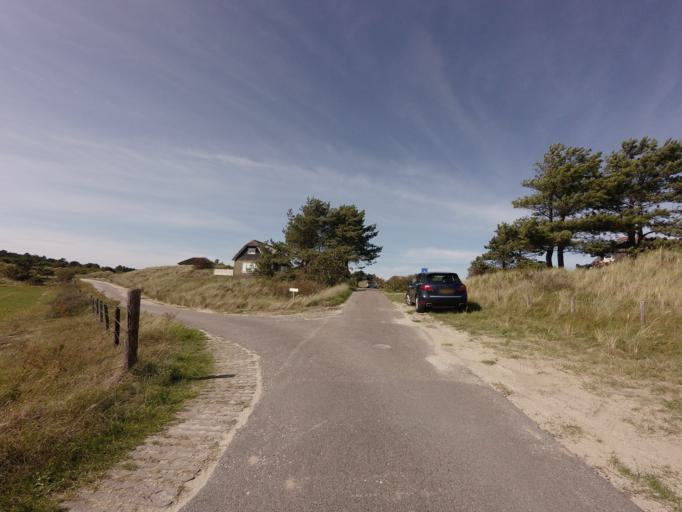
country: NL
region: Friesland
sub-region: Gemeente Ameland
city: Nes
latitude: 53.4539
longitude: 5.7724
